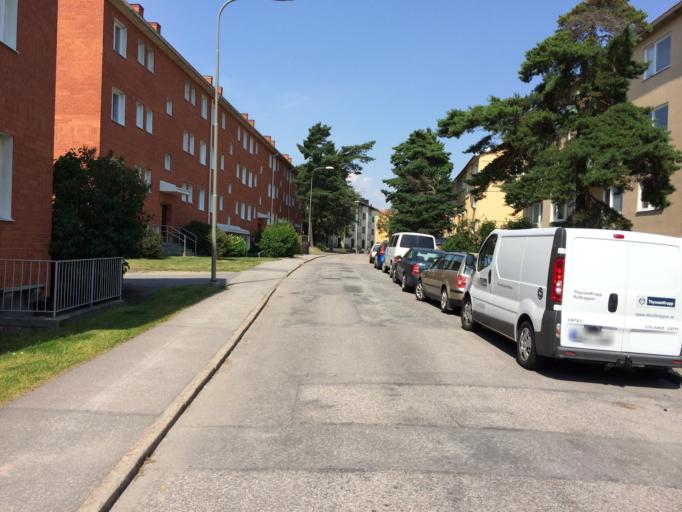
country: SE
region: Stockholm
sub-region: Huddinge Kommun
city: Segeltorp
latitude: 59.2928
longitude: 17.9821
